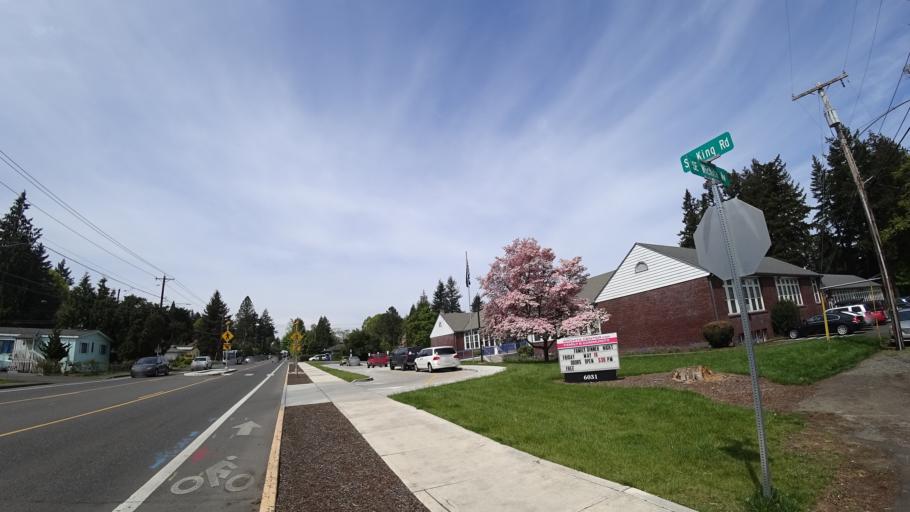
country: US
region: Oregon
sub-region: Clackamas County
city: Oatfield
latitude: 45.4480
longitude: -122.6009
